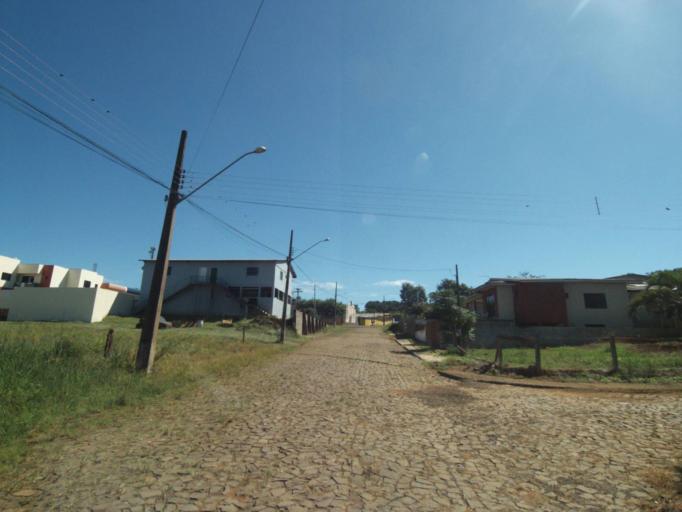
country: BR
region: Parana
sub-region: Pinhao
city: Pinhao
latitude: -25.8367
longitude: -52.0265
